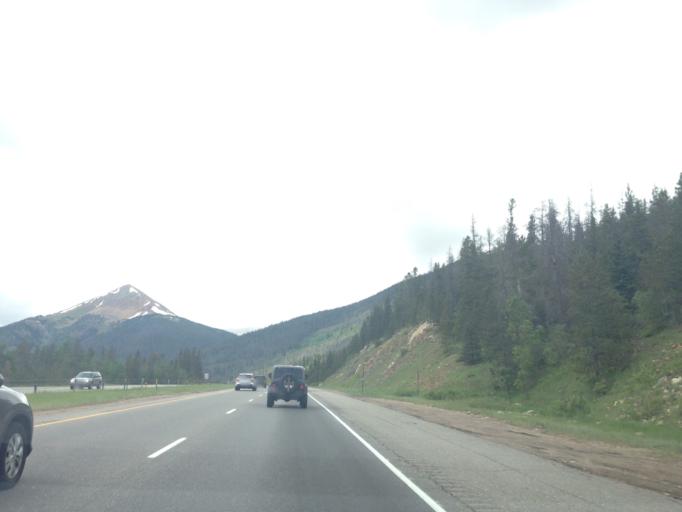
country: US
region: Colorado
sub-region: Clear Creek County
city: Georgetown
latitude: 39.6971
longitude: -105.8300
